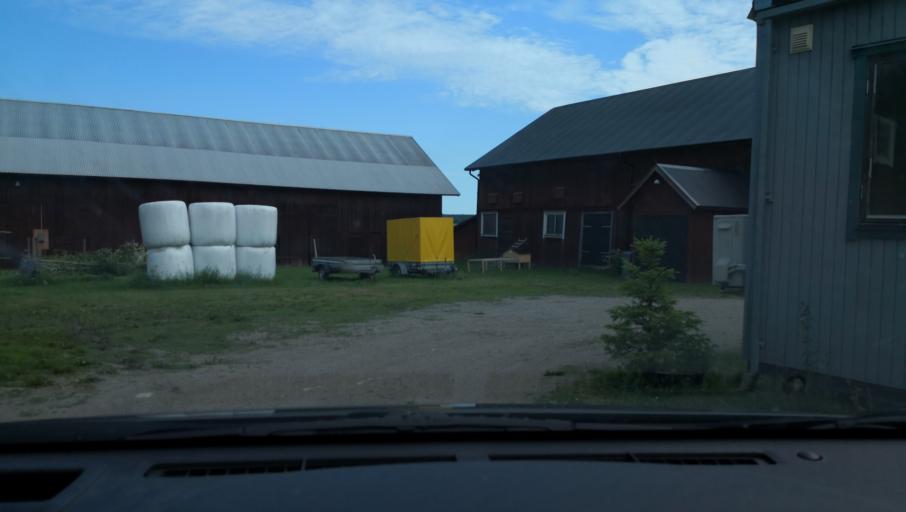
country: SE
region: Uppsala
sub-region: Enkopings Kommun
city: Enkoping
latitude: 59.7040
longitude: 17.1570
